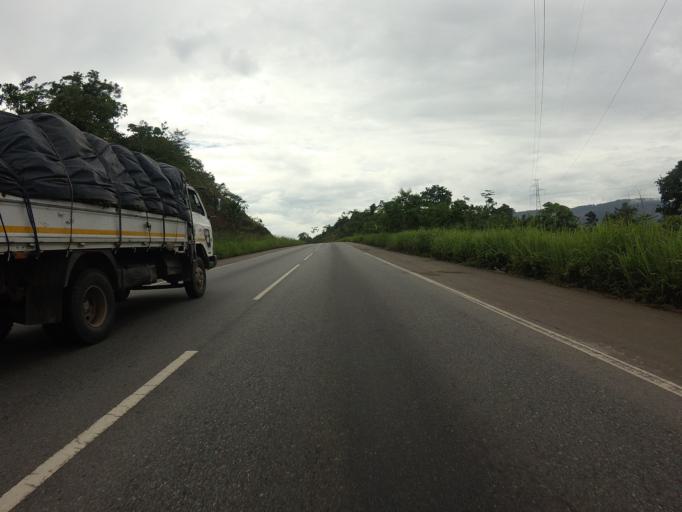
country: GH
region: Eastern
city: Nkawkaw
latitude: 6.5538
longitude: -0.7955
